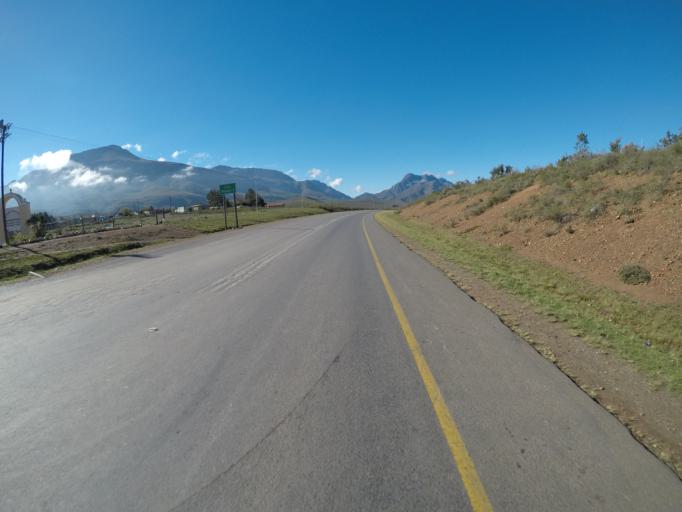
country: ZA
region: Western Cape
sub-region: Overberg District Municipality
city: Caledon
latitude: -34.0493
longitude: 19.5649
